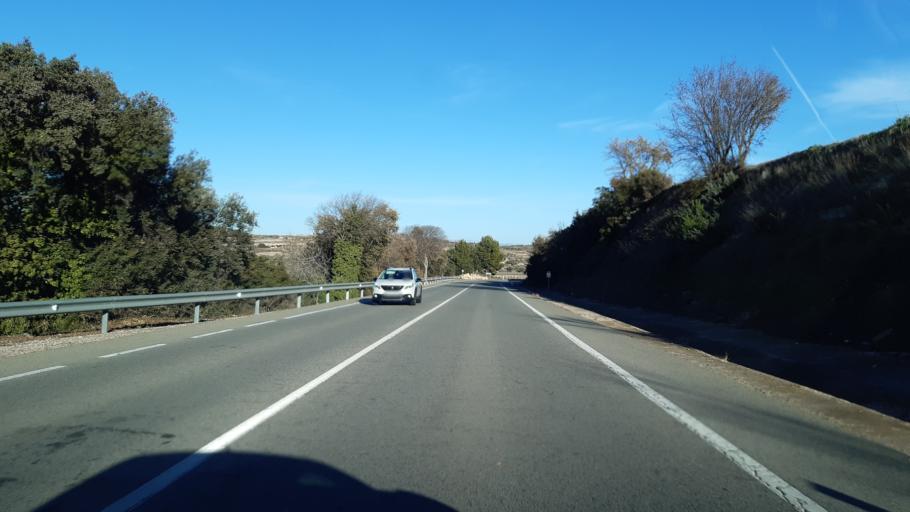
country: ES
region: Catalonia
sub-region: Provincia de Tarragona
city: Gandesa
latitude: 41.0682
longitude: 0.4497
